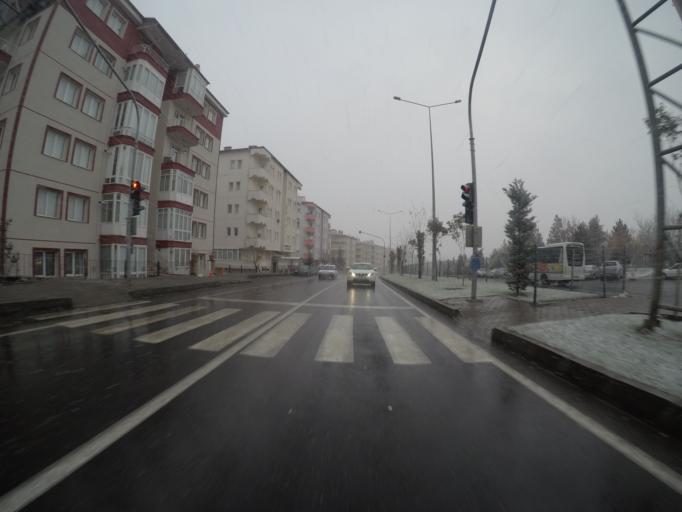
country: TR
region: Nevsehir
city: Nevsehir
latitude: 38.6332
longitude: 34.7294
